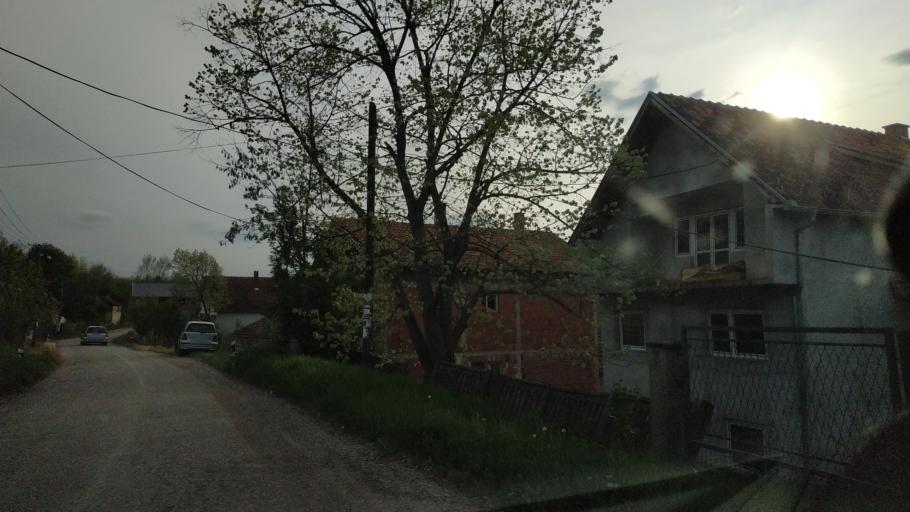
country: RS
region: Central Serbia
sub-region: Nisavski Okrug
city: Aleksinac
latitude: 43.4834
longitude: 21.8175
